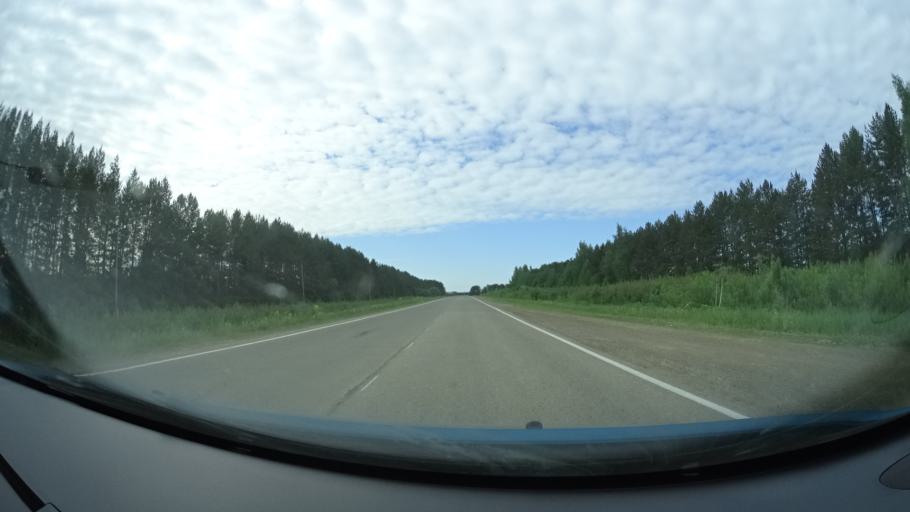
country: RU
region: Perm
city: Kuyeda
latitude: 56.4906
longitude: 55.5987
